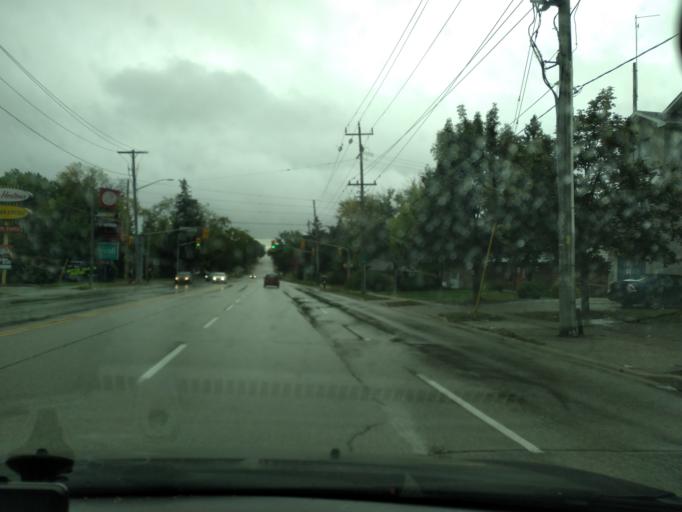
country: CA
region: Ontario
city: Barrie
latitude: 44.4078
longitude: -79.6742
